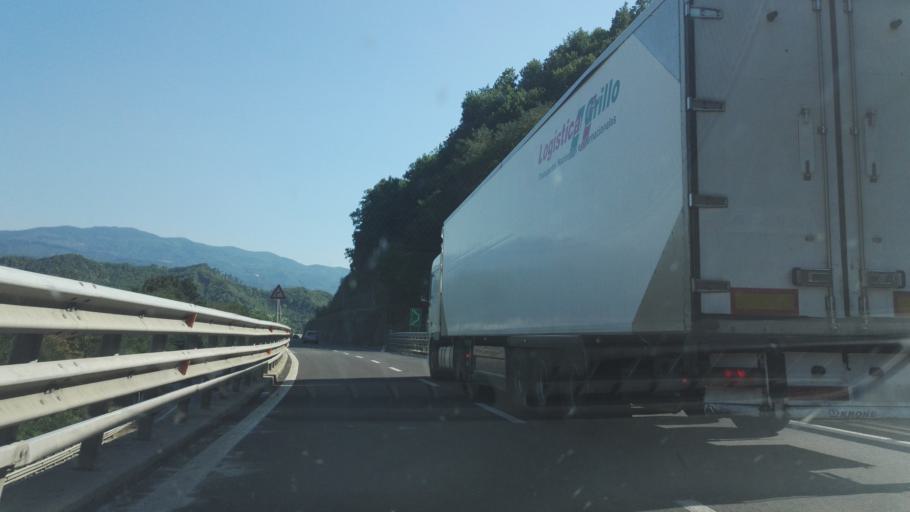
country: IT
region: Calabria
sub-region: Provincia di Cosenza
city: Altilia
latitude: 39.1421
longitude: 16.2742
